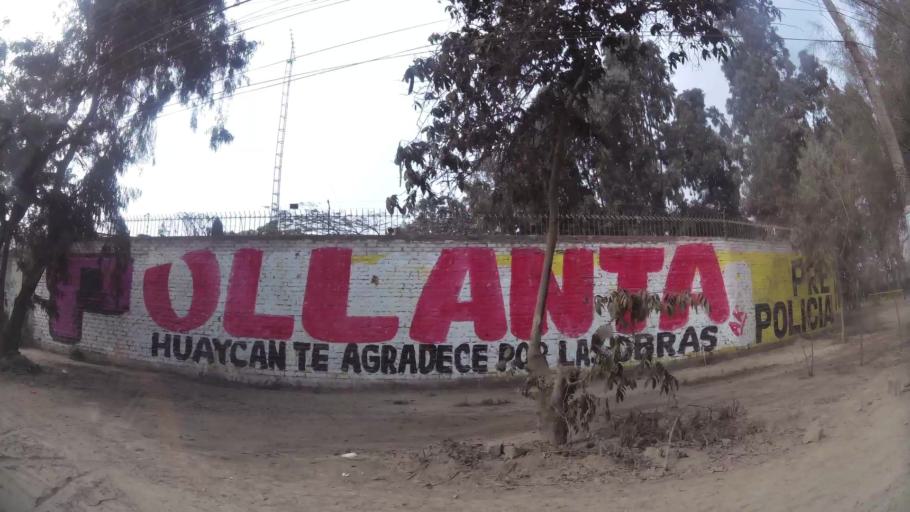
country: PE
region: Lima
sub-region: Lima
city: Santa Maria
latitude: -12.0064
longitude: -76.8353
